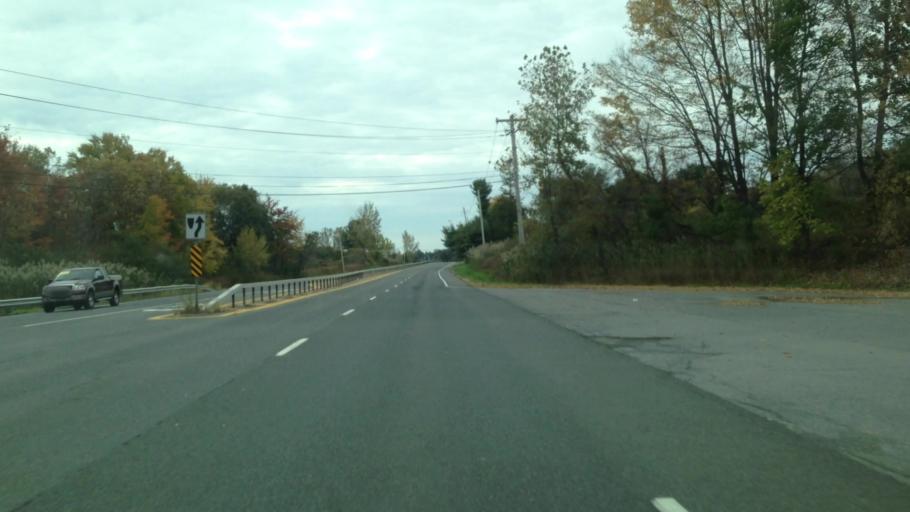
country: US
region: New York
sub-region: Ulster County
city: Highland
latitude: 41.7574
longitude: -73.9625
